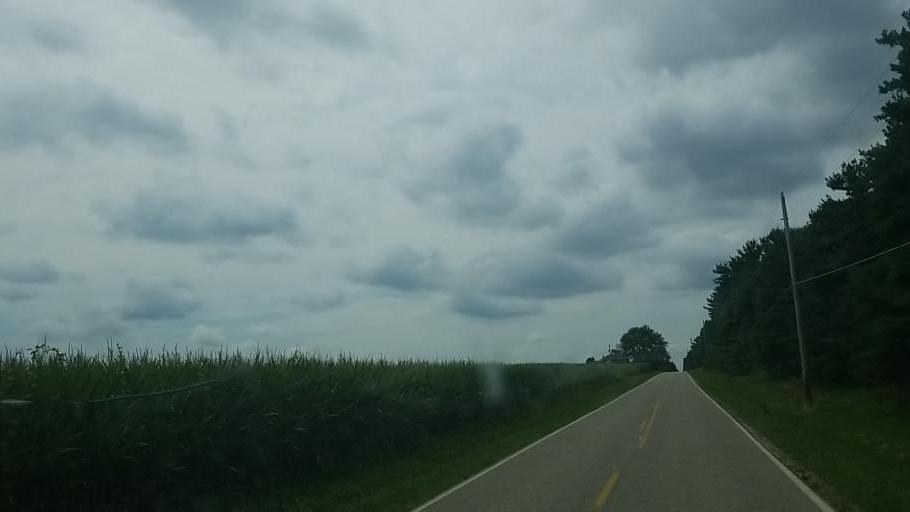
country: US
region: Ohio
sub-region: Fairfield County
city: Lithopolis
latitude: 39.7525
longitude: -82.8534
